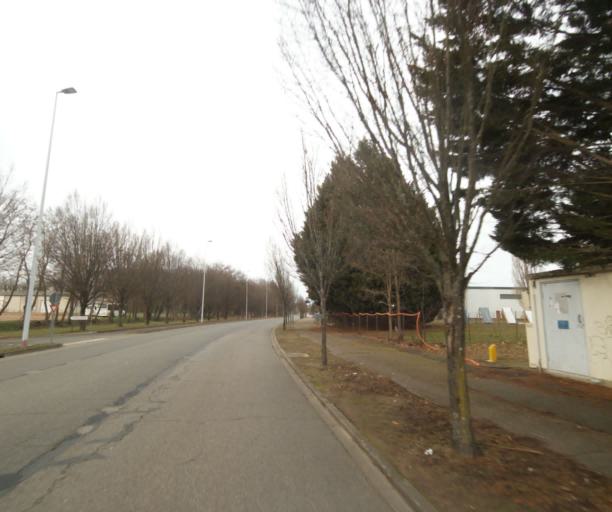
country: FR
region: Rhone-Alpes
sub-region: Departement de la Loire
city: Mably
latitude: 46.0614
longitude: 4.0819
